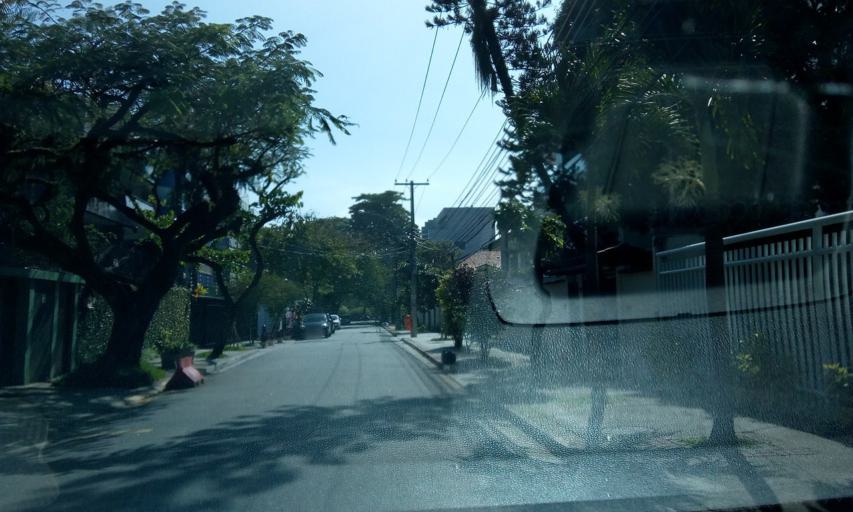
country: BR
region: Rio de Janeiro
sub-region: Nilopolis
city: Nilopolis
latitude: -23.0188
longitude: -43.4589
